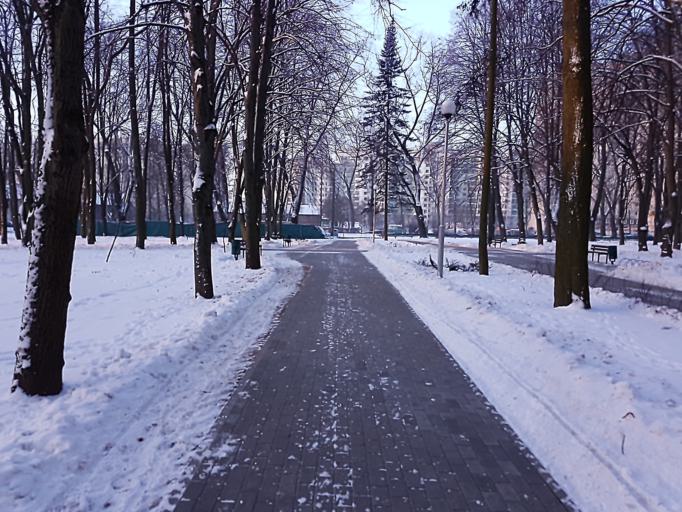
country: BY
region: Minsk
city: Minsk
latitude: 53.8864
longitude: 27.5196
